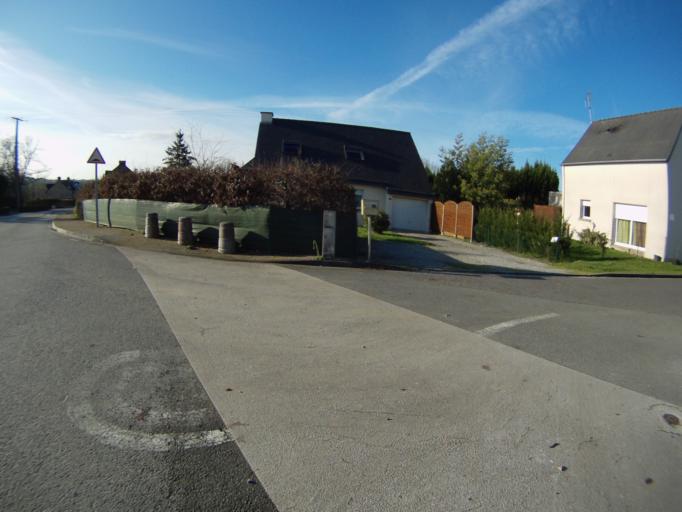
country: FR
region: Brittany
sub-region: Departement d'Ille-et-Vilaine
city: Chanteloup
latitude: 47.9277
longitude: -1.6118
